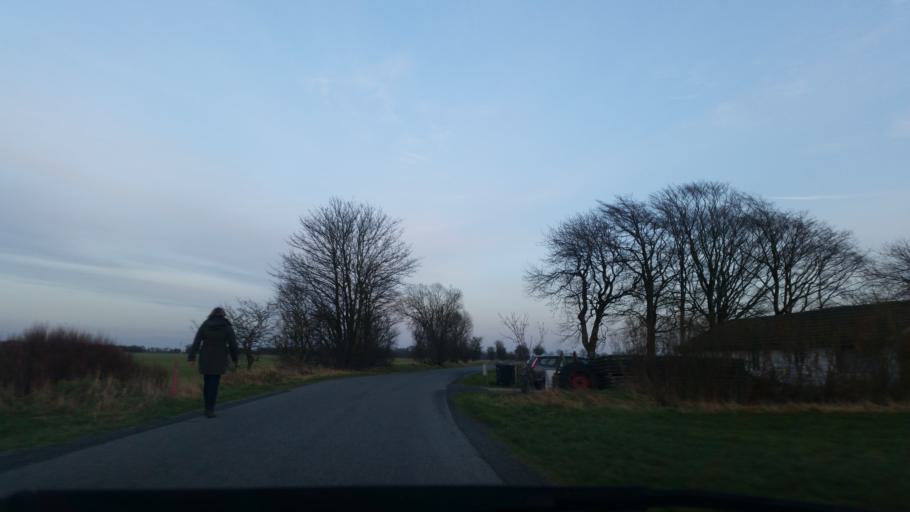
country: DK
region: South Denmark
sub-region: Esbjerg Kommune
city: Ribe
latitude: 55.3870
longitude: 8.8842
